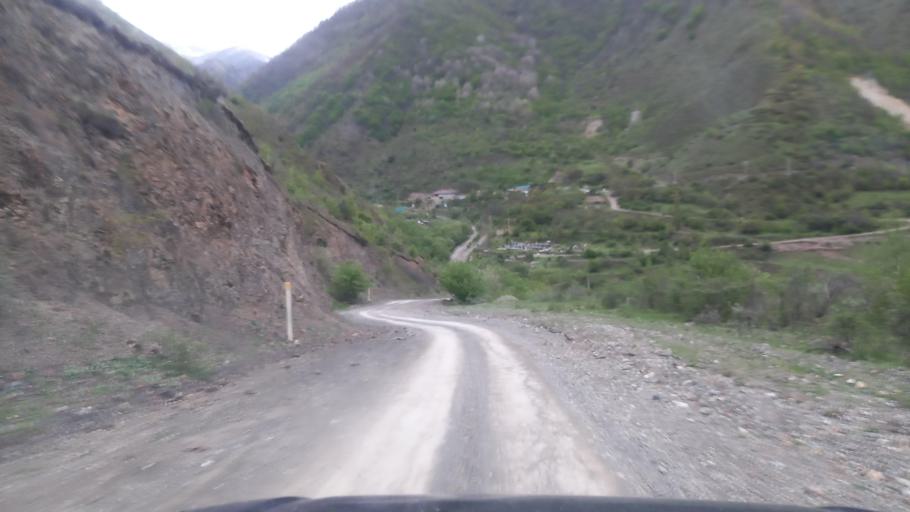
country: RU
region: North Ossetia
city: Mizur
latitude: 42.8516
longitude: 44.1582
